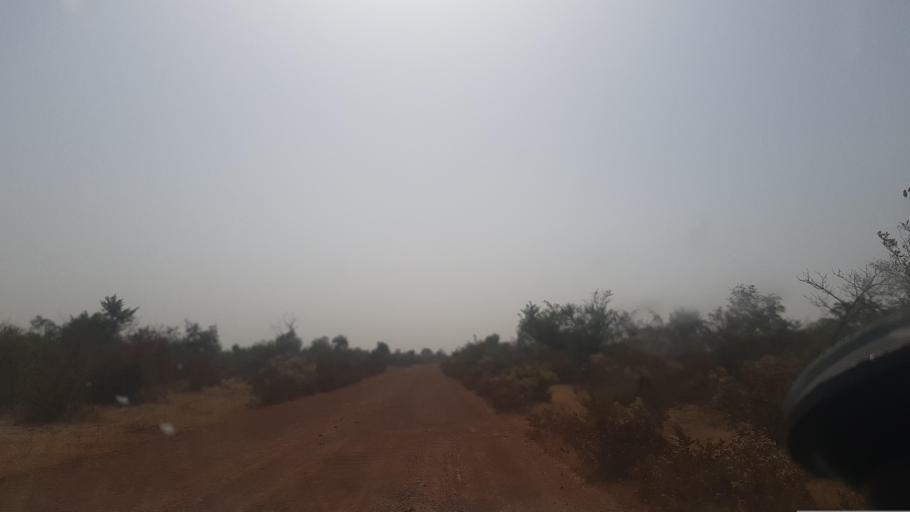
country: ML
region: Segou
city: Baroueli
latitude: 13.0630
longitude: -6.4744
